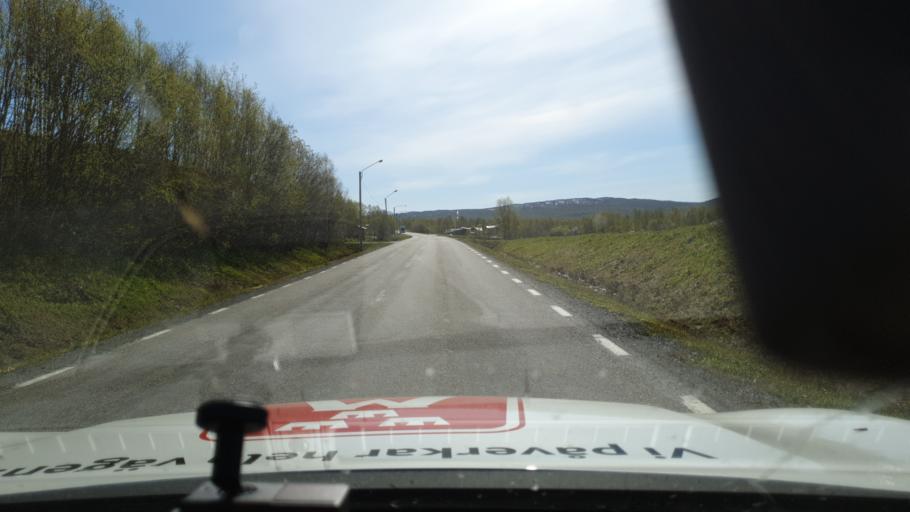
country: NO
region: Nordland
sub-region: Hattfjelldal
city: Hattfjelldal
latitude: 65.7524
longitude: 14.9579
